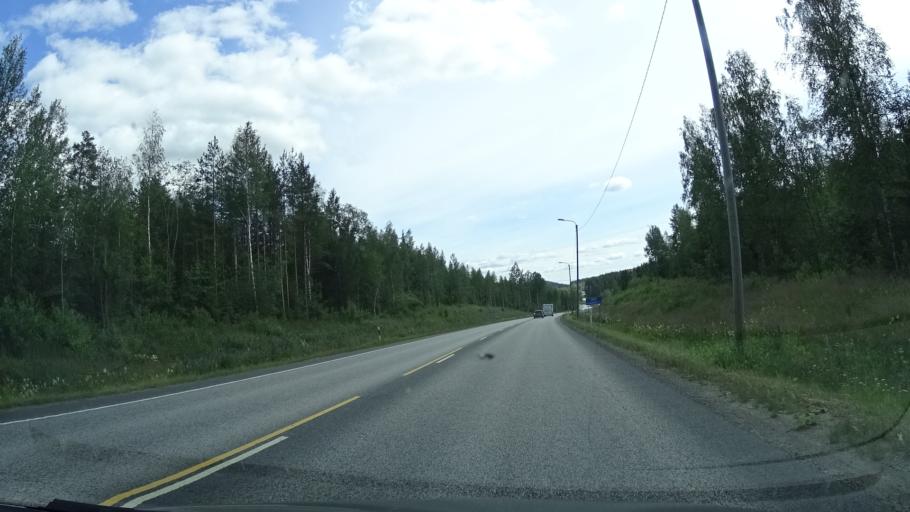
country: FI
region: Central Finland
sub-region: Jyvaeskylae
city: Jyvaeskylae
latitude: 62.2599
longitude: 25.6032
